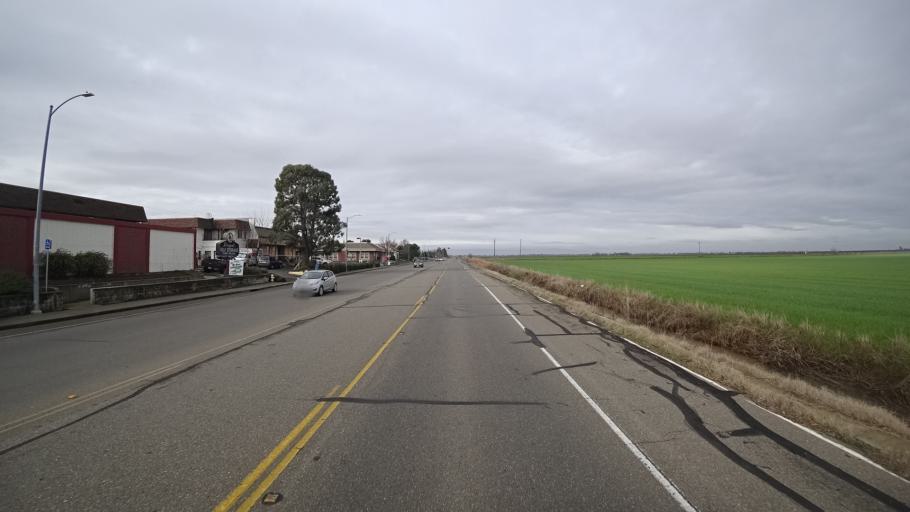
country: US
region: California
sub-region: Yolo County
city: Davis
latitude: 38.5611
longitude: -121.7839
